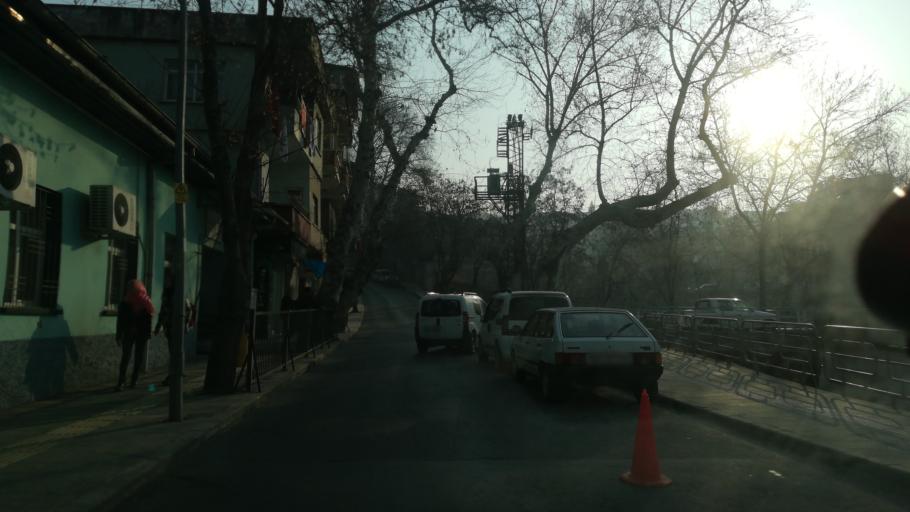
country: TR
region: Kahramanmaras
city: Kahramanmaras
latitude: 37.5865
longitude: 36.9288
